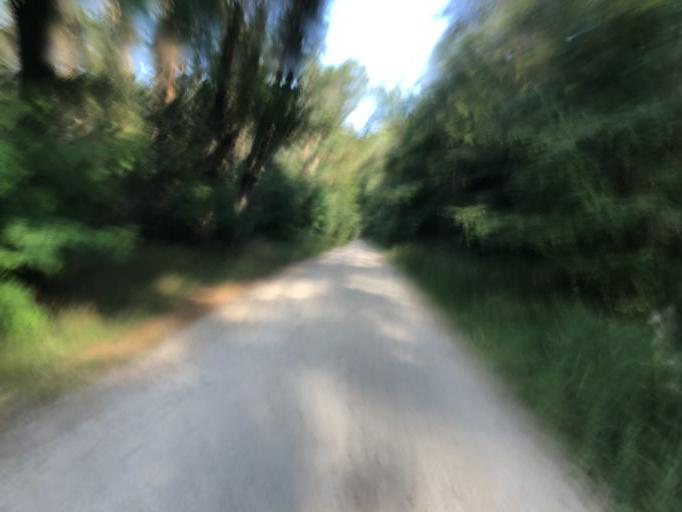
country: DE
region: Bavaria
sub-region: Regierungsbezirk Mittelfranken
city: Uttenreuth
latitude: 49.5678
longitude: 11.0836
